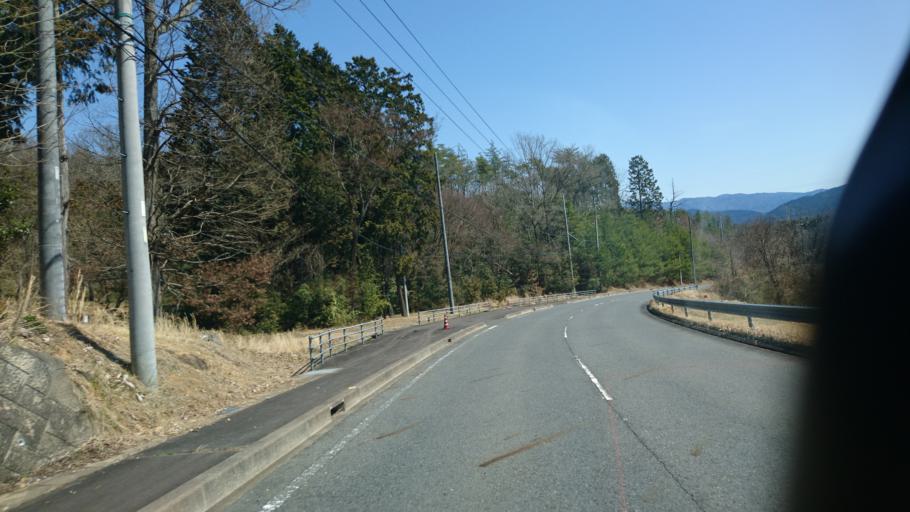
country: JP
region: Gifu
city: Nakatsugawa
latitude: 35.4603
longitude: 137.3651
